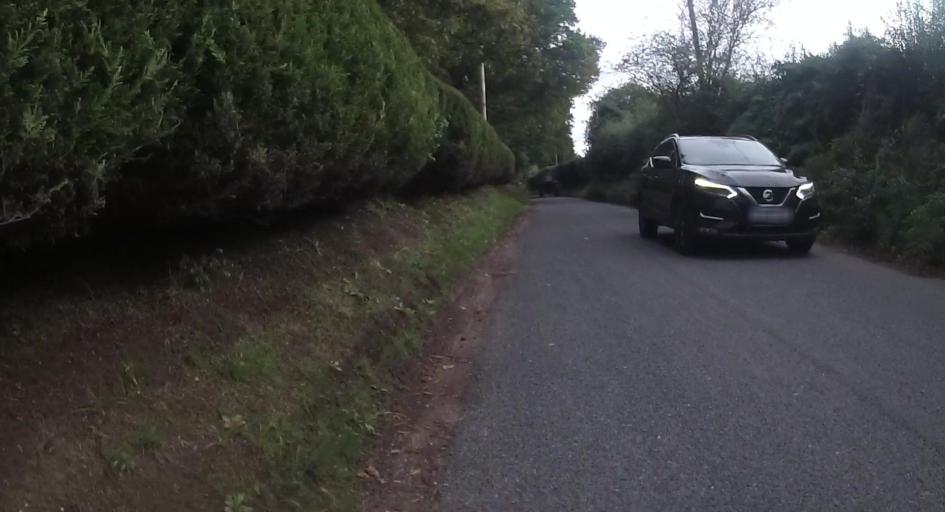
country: GB
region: England
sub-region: Hampshire
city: Hook
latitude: 51.3096
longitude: -0.9325
